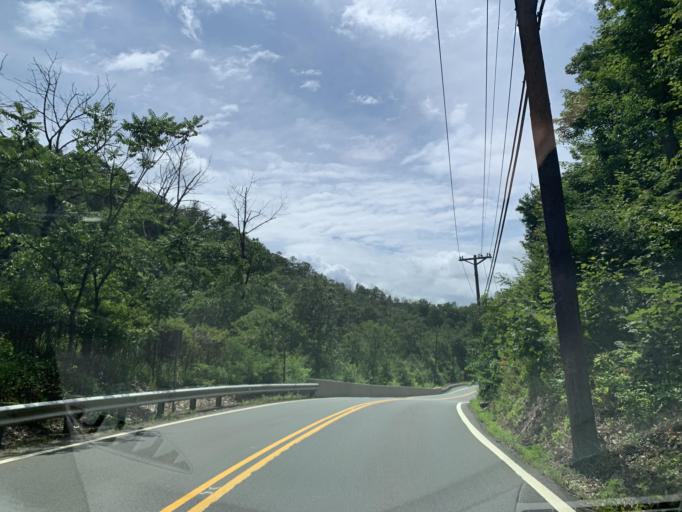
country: US
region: New Jersey
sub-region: Somerset County
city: Martinsville
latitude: 40.5867
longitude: -74.5620
